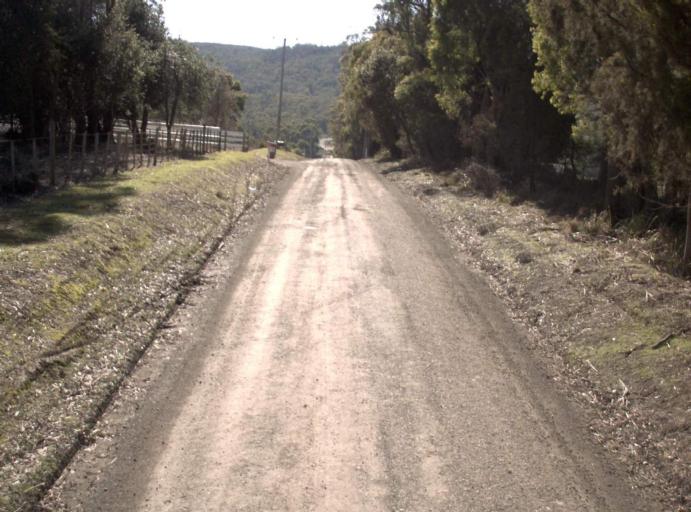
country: AU
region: Tasmania
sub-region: Launceston
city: Mayfield
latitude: -41.2803
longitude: 147.0435
